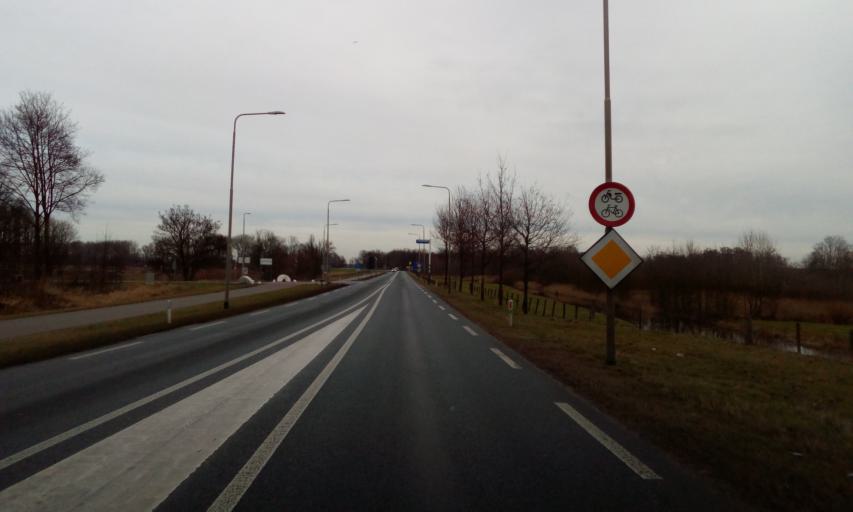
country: NL
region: North Brabant
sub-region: Gemeente Woudrichem
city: Woudrichem
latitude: 51.7961
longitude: 5.0547
